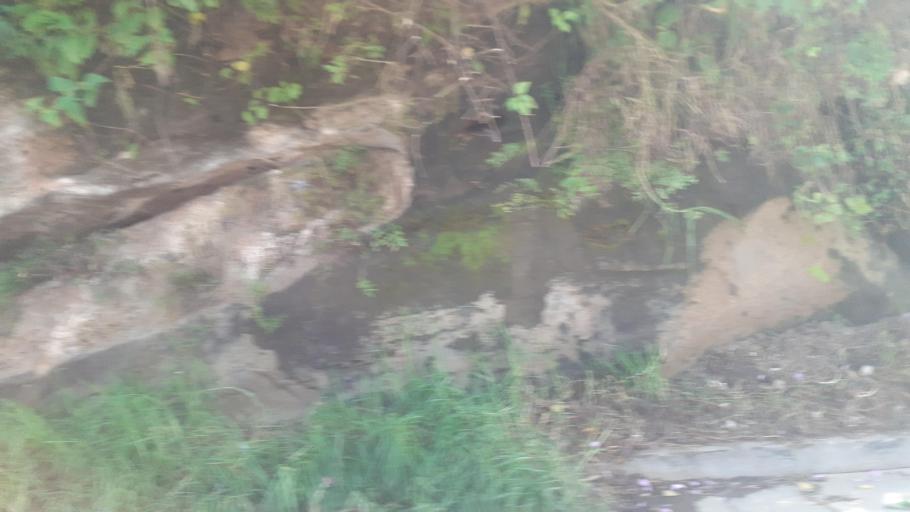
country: GT
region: Quetzaltenango
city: Cantel
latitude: 14.8148
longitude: -91.4509
